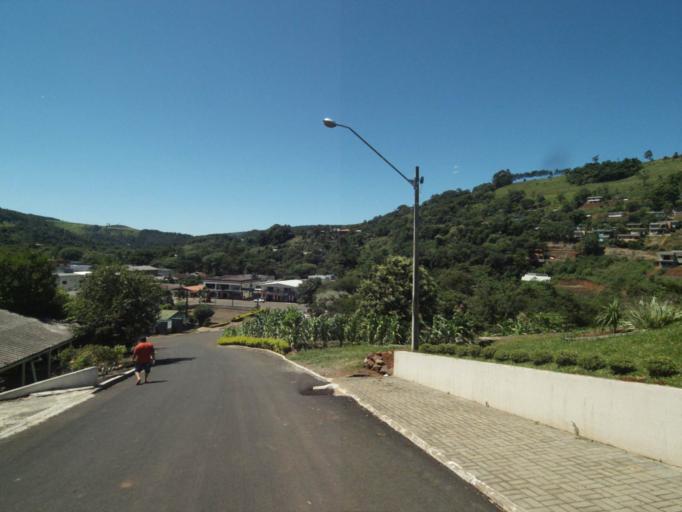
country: BR
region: Parana
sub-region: Ampere
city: Ampere
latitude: -26.1747
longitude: -53.3603
